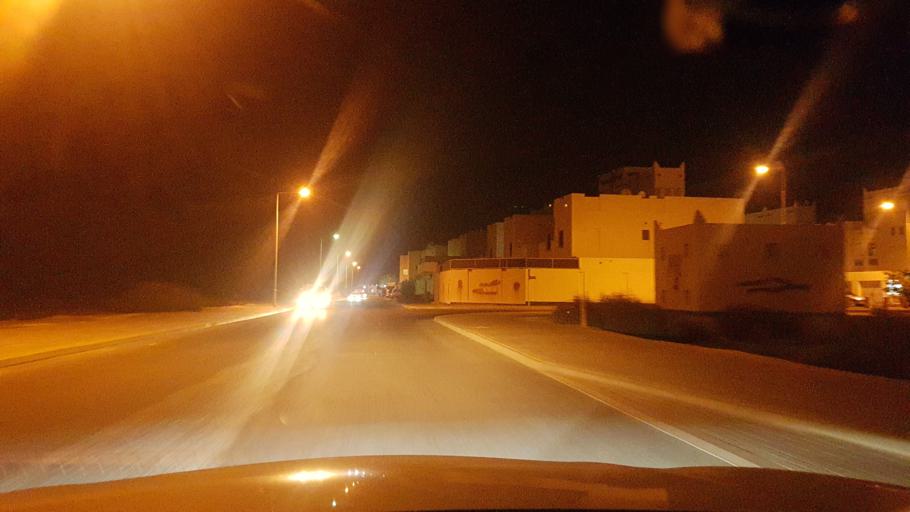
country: BH
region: Central Governorate
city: Madinat Hamad
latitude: 26.0944
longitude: 50.4819
